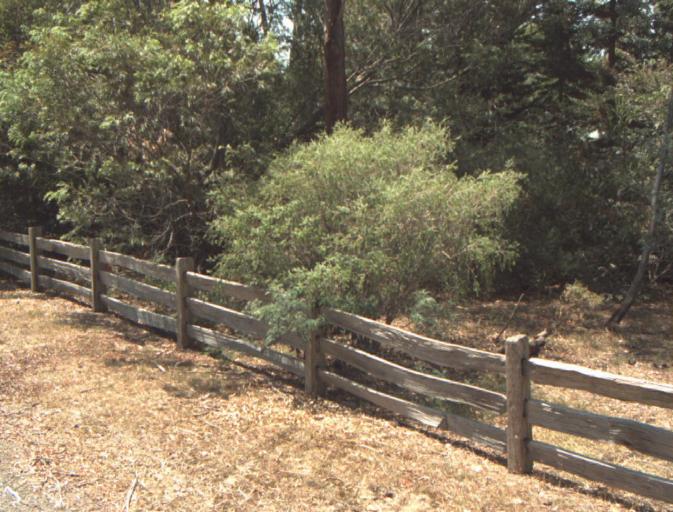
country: AU
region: Tasmania
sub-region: Launceston
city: Newstead
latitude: -41.4917
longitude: 147.1954
